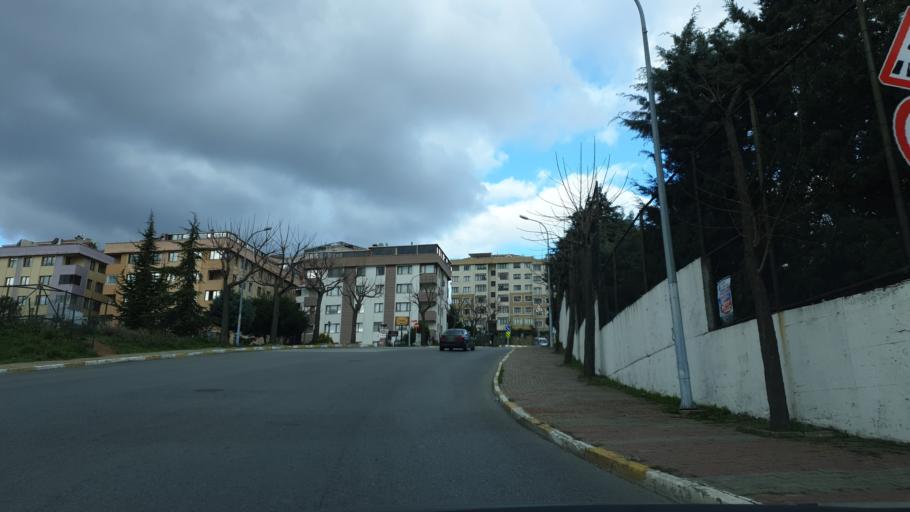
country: TR
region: Istanbul
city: Pendik
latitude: 40.9002
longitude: 29.2454
